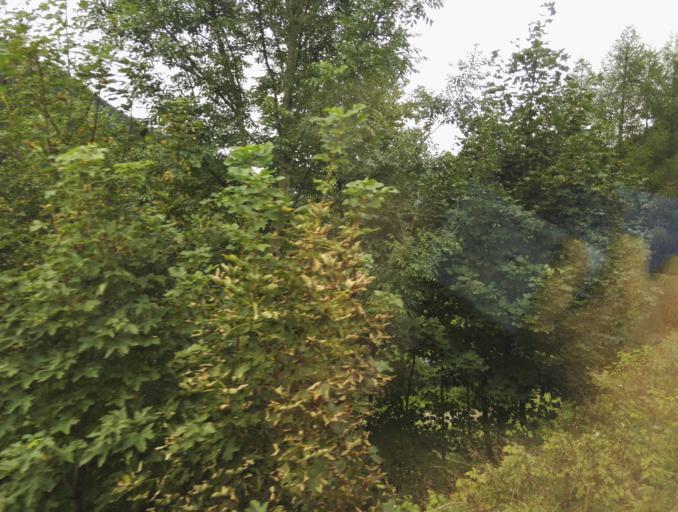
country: AT
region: Styria
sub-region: Politischer Bezirk Leoben
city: Vordernberg
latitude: 47.4983
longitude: 14.9929
